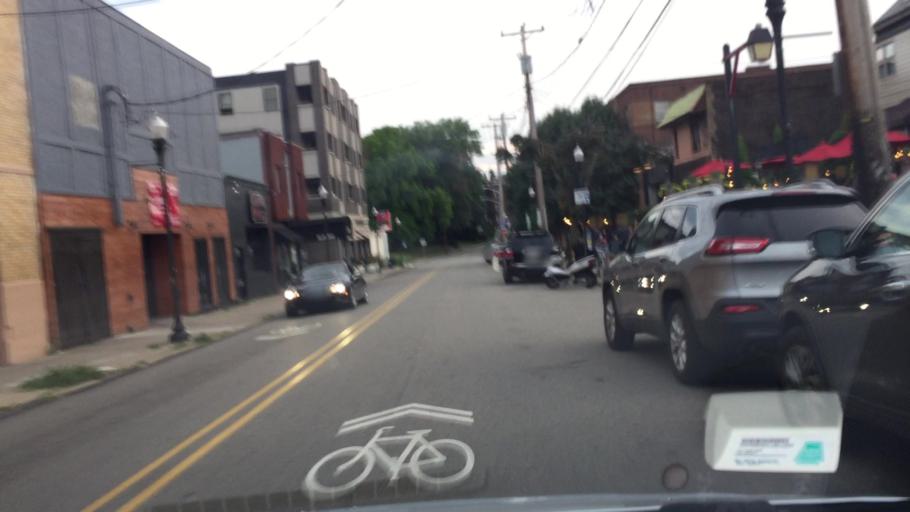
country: US
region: Pennsylvania
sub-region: Allegheny County
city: Bloomfield
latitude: 40.4560
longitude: -79.9309
